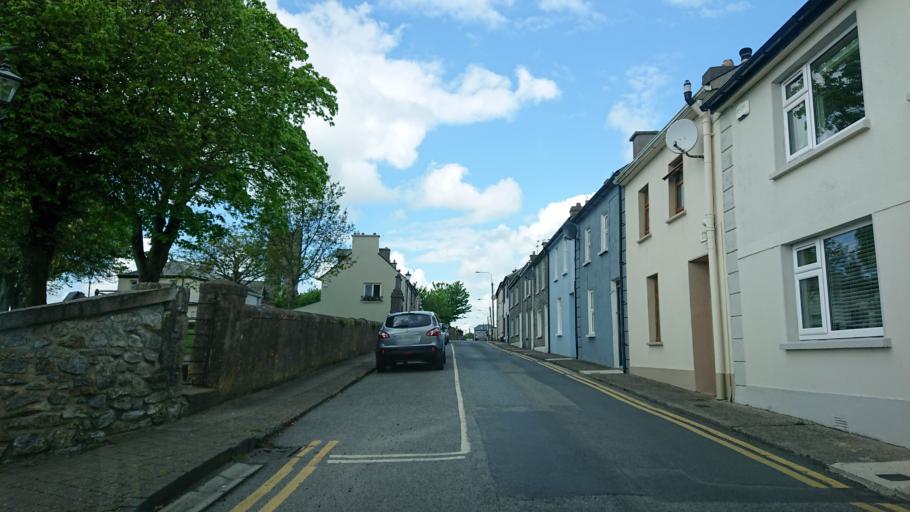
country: IE
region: Munster
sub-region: Waterford
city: Dungarvan
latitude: 52.0874
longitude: -7.6164
